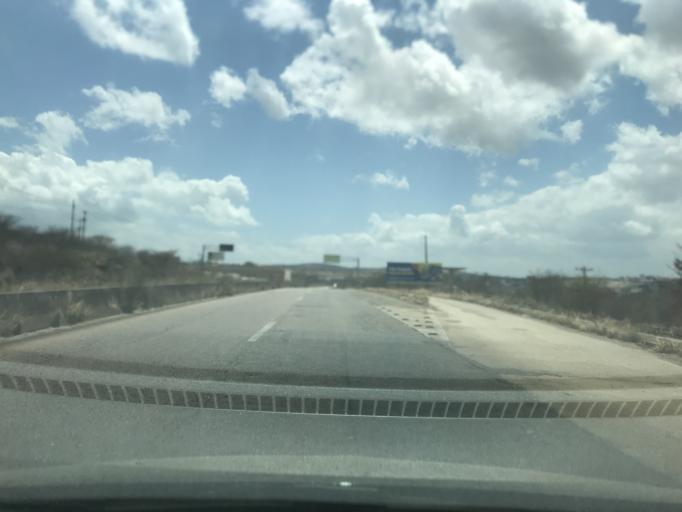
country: BR
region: Pernambuco
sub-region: Caruaru
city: Caruaru
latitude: -8.3079
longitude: -35.9452
